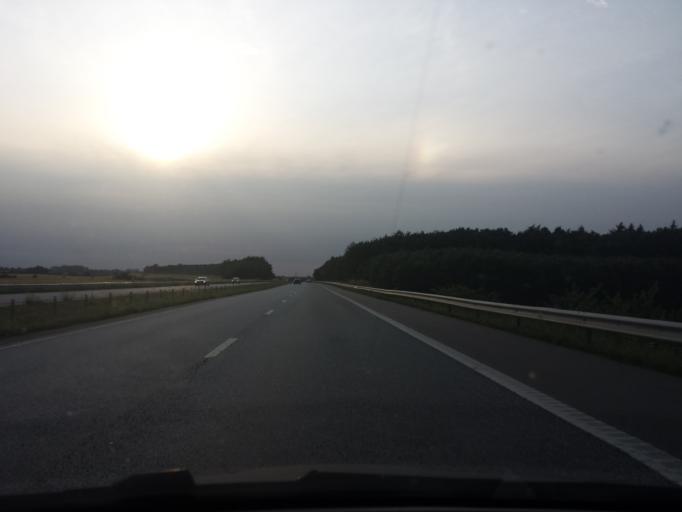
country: SE
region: Skane
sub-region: Malmo
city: Oxie
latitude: 55.5448
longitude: 13.1486
